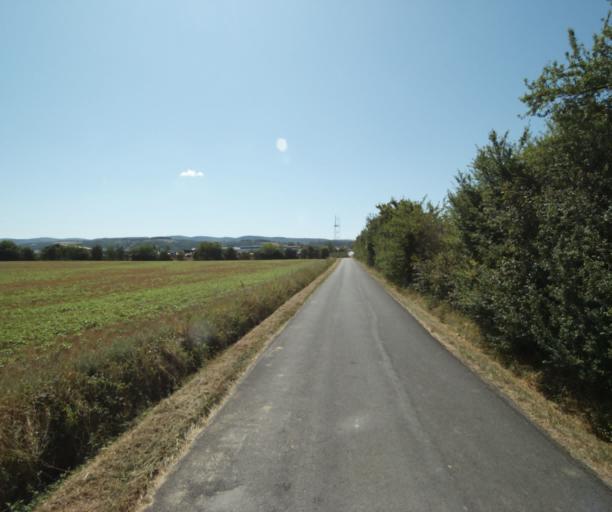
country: FR
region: Midi-Pyrenees
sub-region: Departement de la Haute-Garonne
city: Revel
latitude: 43.4580
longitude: 1.9734
